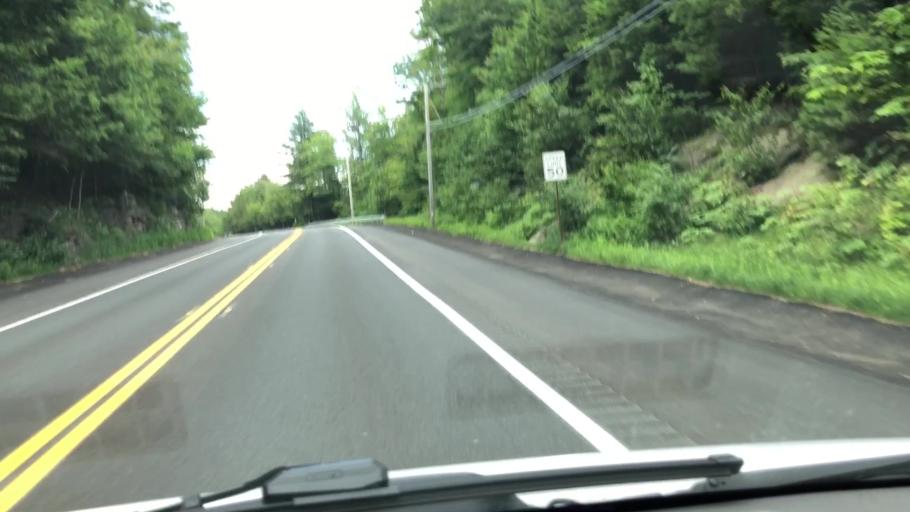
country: US
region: Massachusetts
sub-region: Hampshire County
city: Chesterfield
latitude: 42.4491
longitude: -72.8180
